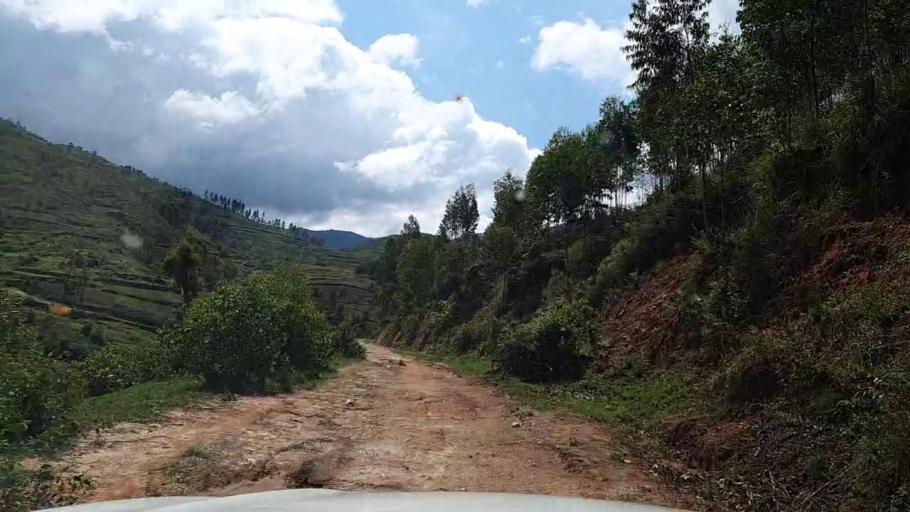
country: RW
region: Southern Province
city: Gikongoro
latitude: -2.3610
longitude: 29.5341
